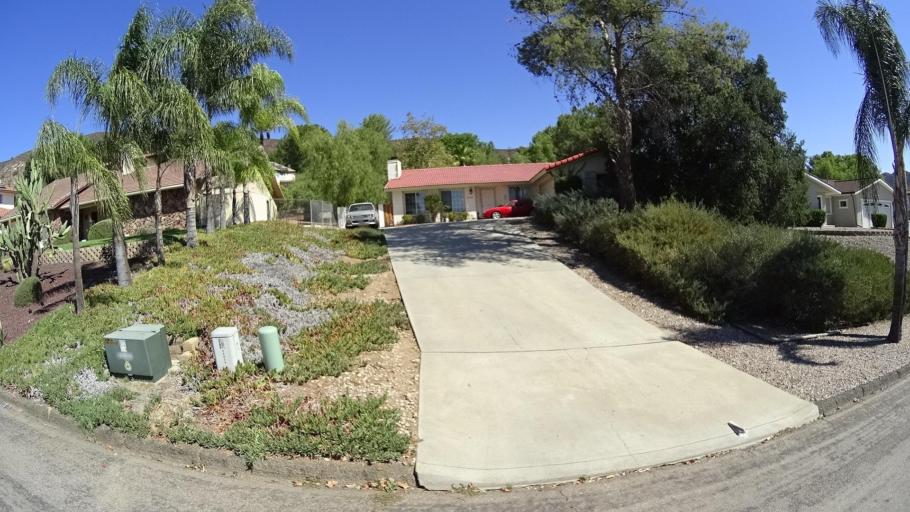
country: US
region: California
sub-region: San Diego County
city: San Diego Country Estates
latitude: 33.0265
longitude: -116.8017
